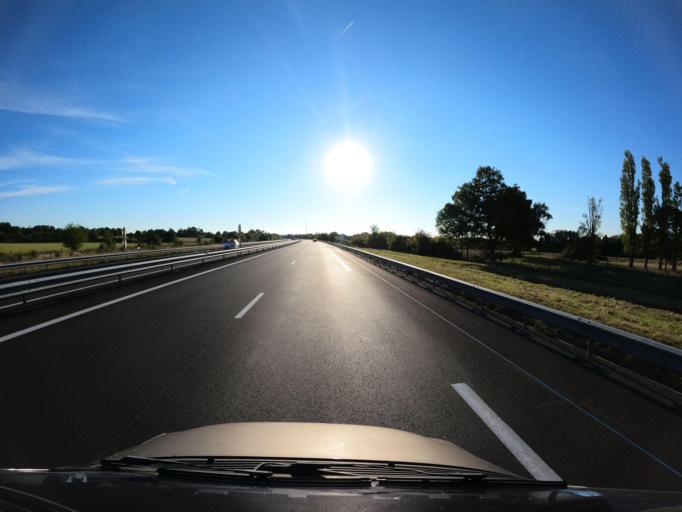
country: FR
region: Pays de la Loire
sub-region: Departement de Maine-et-Loire
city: La Tessoualle
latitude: 47.0099
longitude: -0.8941
